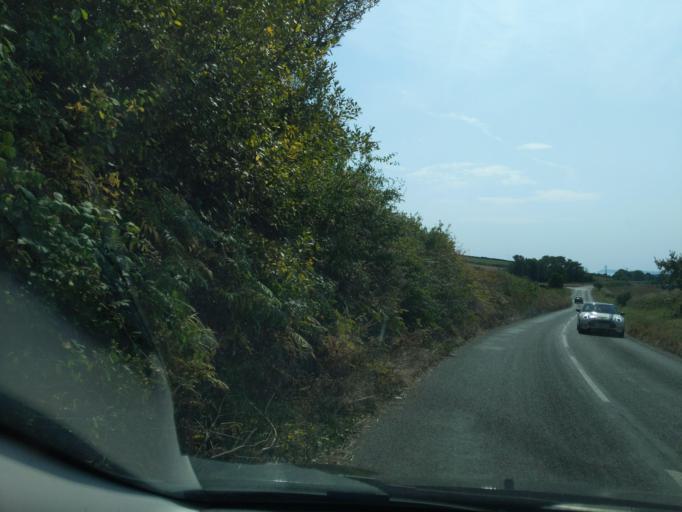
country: GB
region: England
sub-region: Cornwall
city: Fowey
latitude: 50.3470
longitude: -4.6165
